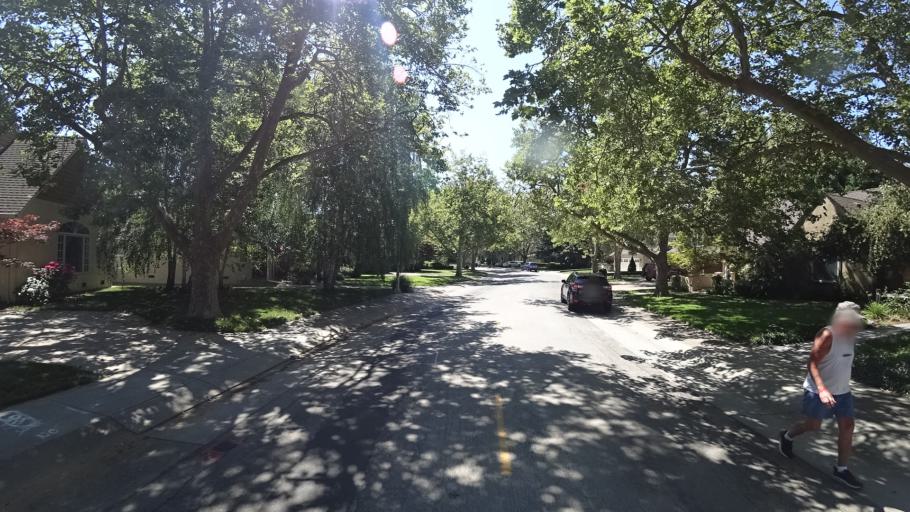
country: US
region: California
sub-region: Sacramento County
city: Sacramento
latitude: 38.5475
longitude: -121.5019
